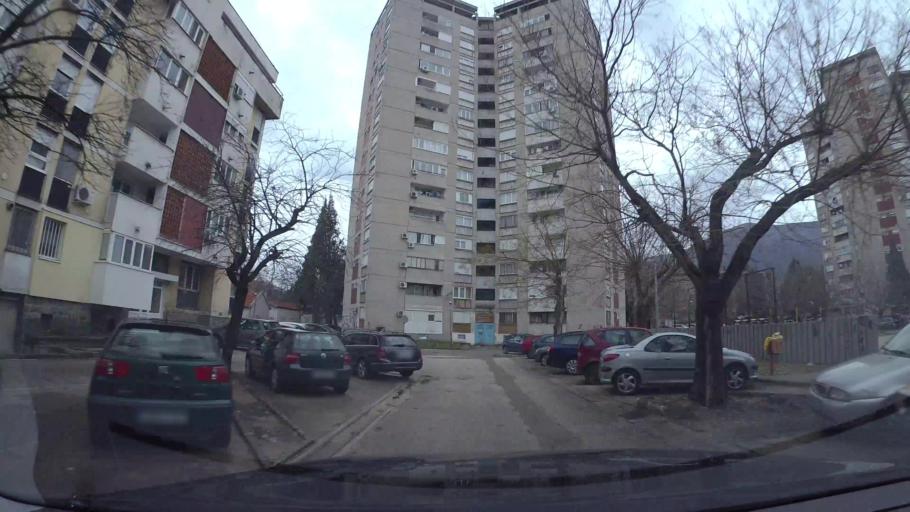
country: BA
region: Federation of Bosnia and Herzegovina
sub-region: Hercegovacko-Bosanski Kanton
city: Mostar
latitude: 43.3486
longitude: 17.8018
